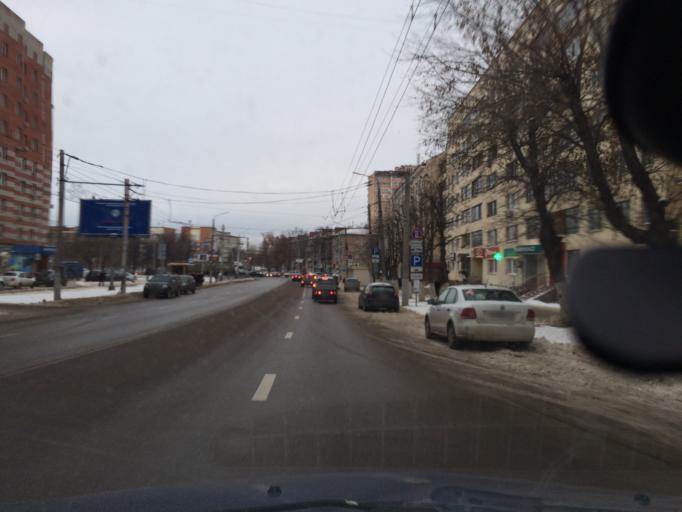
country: RU
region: Tula
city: Tula
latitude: 54.1970
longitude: 37.5850
